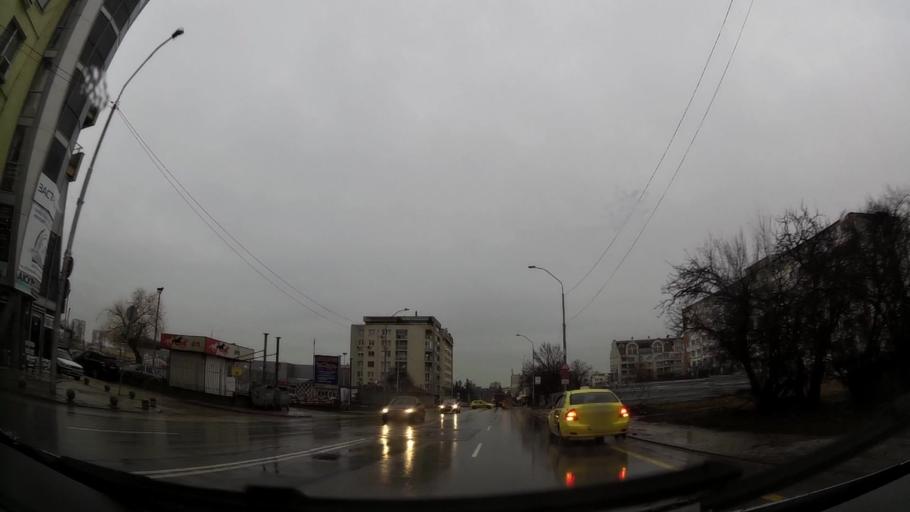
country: BG
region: Sofia-Capital
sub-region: Stolichna Obshtina
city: Sofia
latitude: 42.6578
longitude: 23.3489
